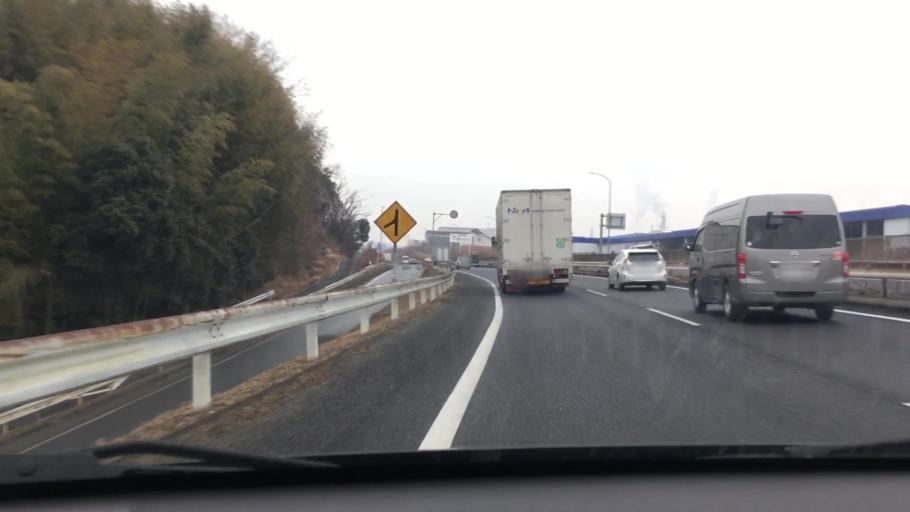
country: JP
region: Mie
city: Ueno-ebisumachi
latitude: 34.7065
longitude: 136.0759
